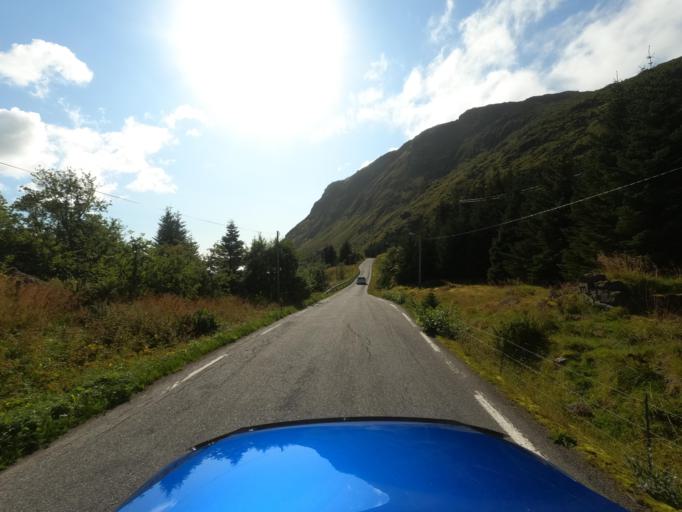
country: NO
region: Nordland
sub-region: Vestvagoy
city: Evjen
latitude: 68.1381
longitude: 13.7421
